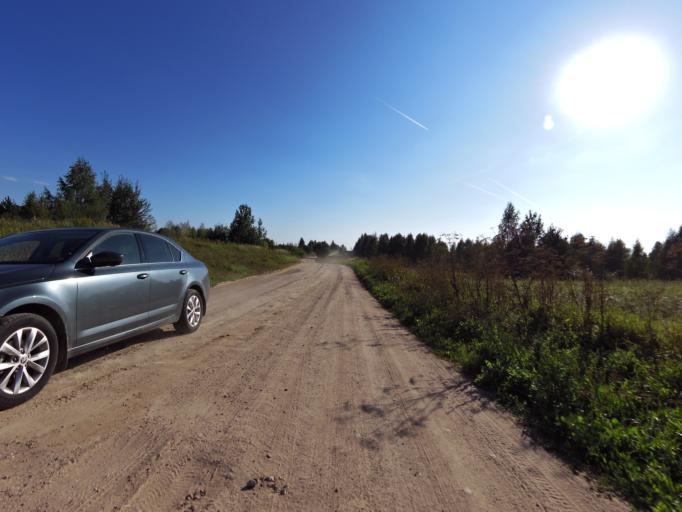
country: LT
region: Vilnius County
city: Pilaite
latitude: 54.7152
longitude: 25.1773
